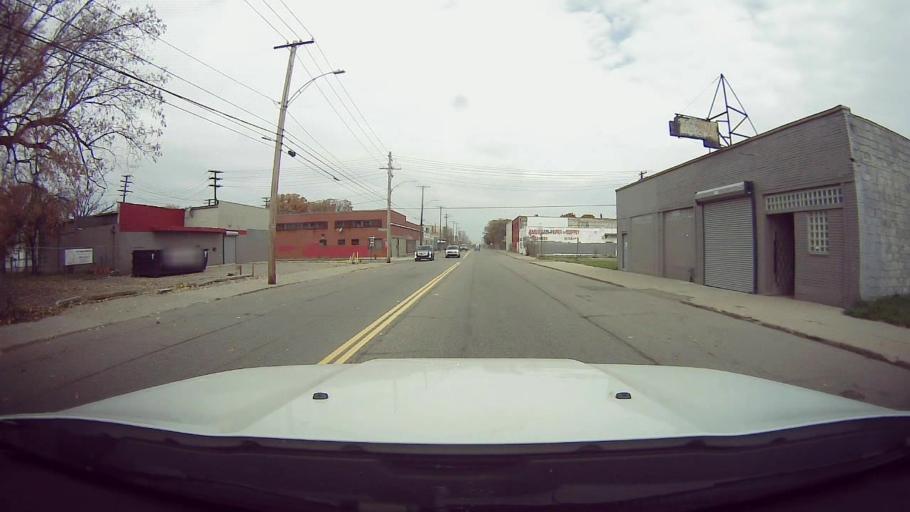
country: US
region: Michigan
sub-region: Wayne County
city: Highland Park
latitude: 42.4286
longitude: -83.1022
